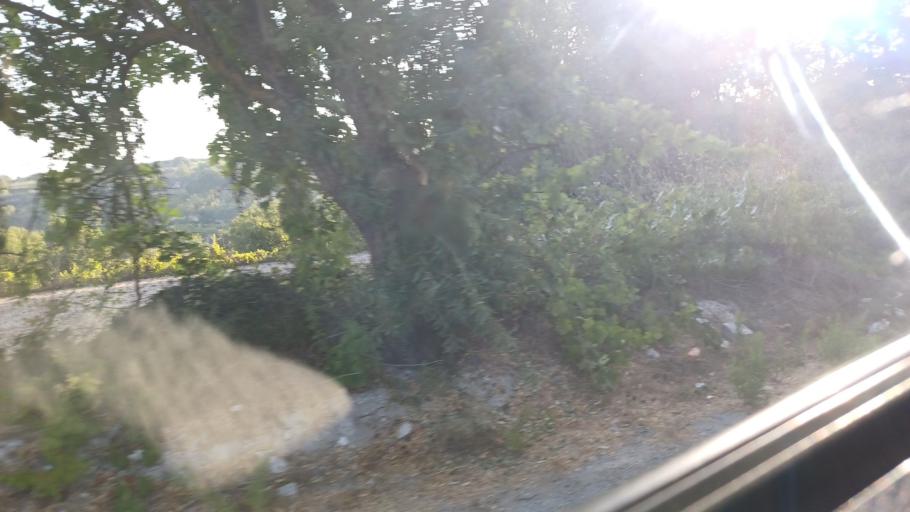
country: CY
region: Pafos
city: Mesogi
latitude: 34.8350
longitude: 32.4810
